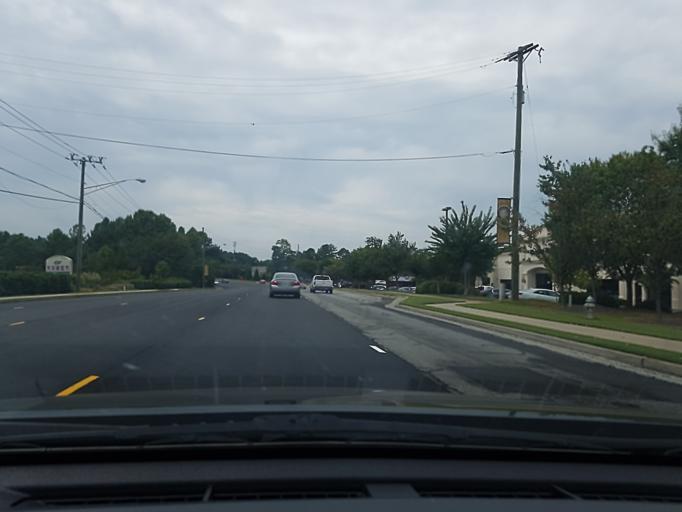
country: US
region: Georgia
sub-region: Gwinnett County
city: Duluth
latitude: 33.9657
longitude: -84.1344
